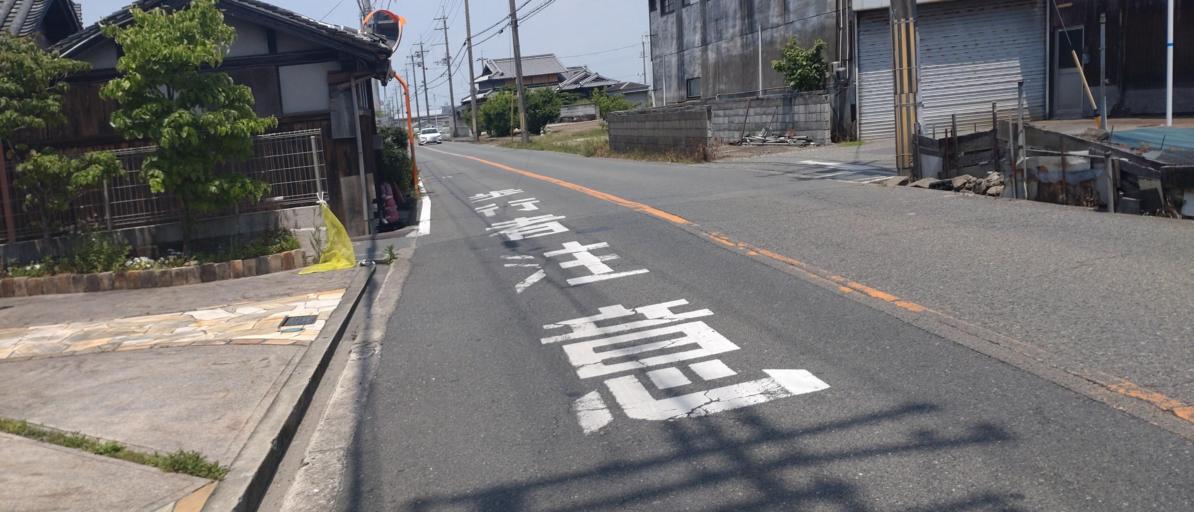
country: JP
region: Osaka
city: Matsubara
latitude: 34.5227
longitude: 135.5572
